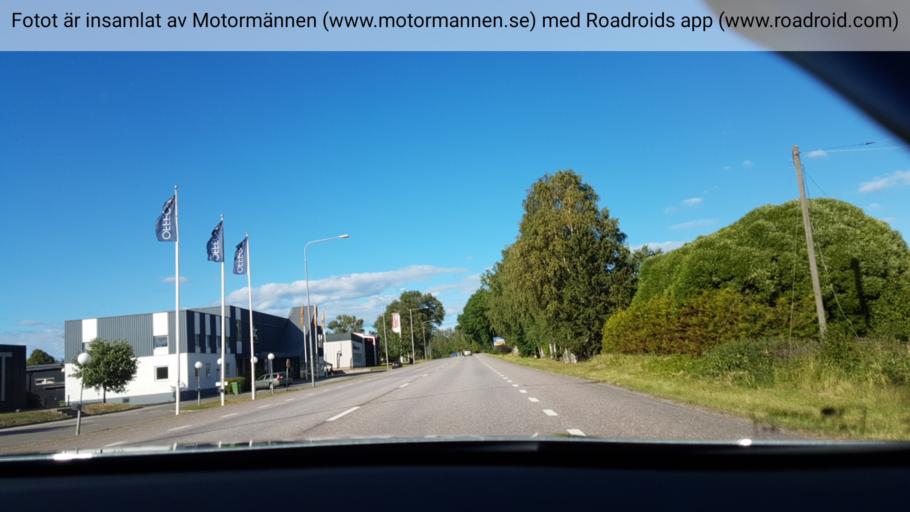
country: SE
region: Vaestra Goetaland
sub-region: Tibro Kommun
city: Tibro
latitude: 58.4233
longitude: 14.1359
